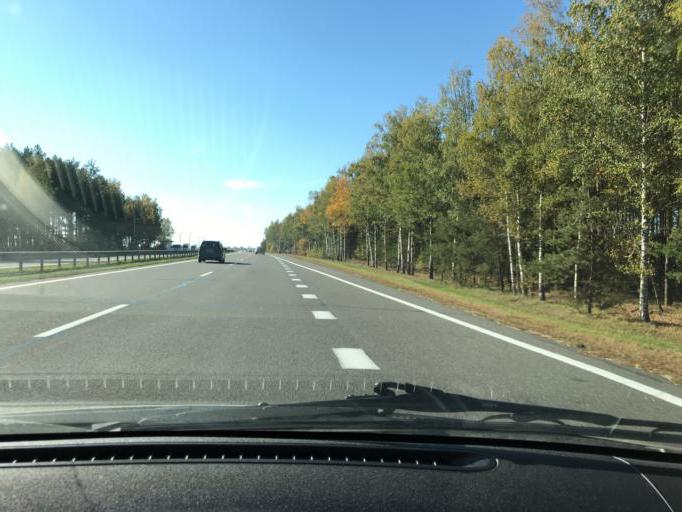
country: BY
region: Brest
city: Ivatsevichy
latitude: 52.7109
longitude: 25.3901
